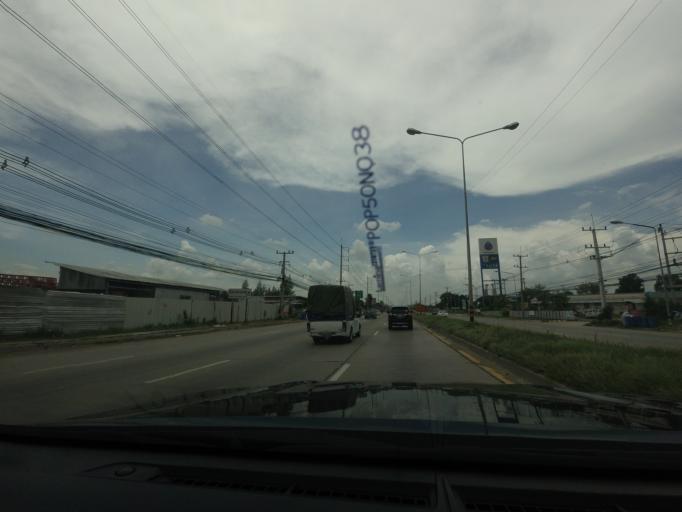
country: TH
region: Nakhon Pathom
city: Nakhon Pathom
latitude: 13.8549
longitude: 100.0156
